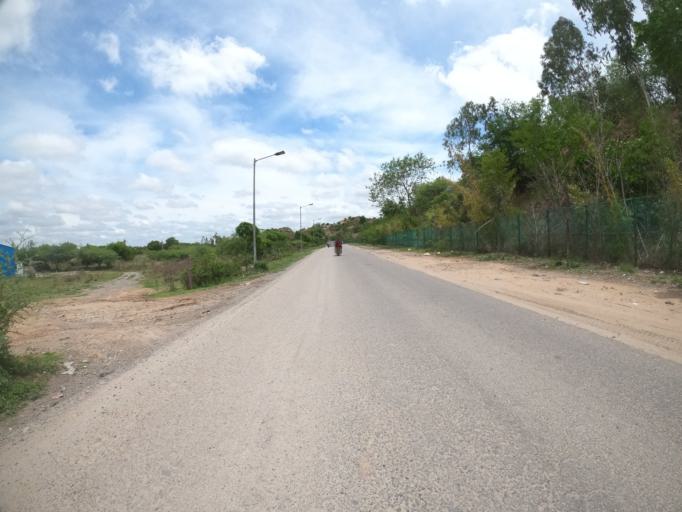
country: IN
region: Telangana
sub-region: Hyderabad
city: Hyderabad
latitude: 17.3099
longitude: 78.3763
